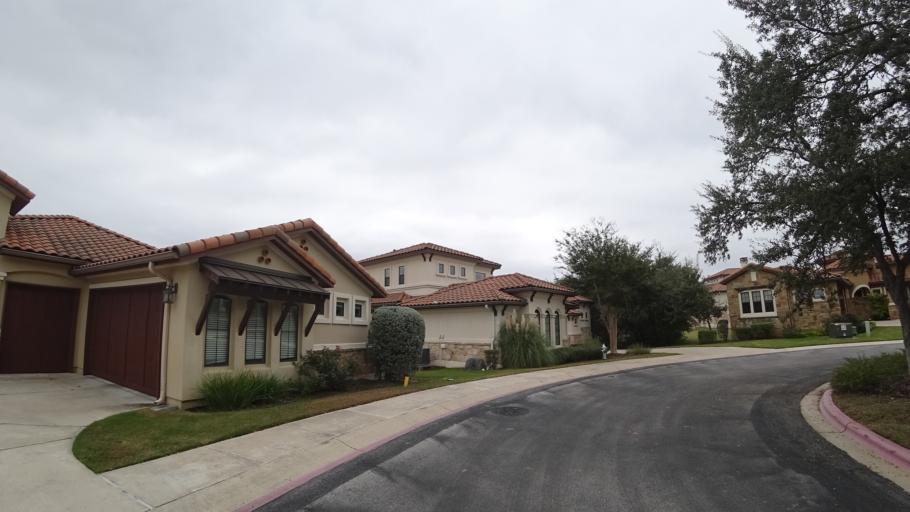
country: US
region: Texas
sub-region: Travis County
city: Bee Cave
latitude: 30.3489
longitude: -97.9089
